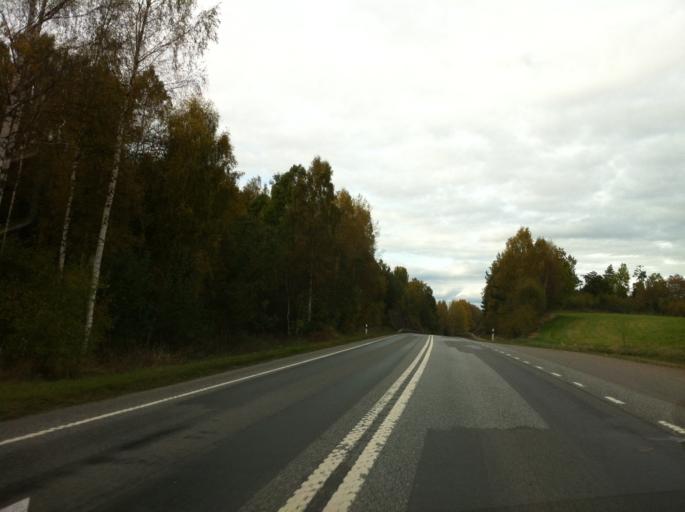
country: SE
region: OEstergoetland
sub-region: Motala Kommun
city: Ryd
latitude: 58.6646
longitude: 14.9660
